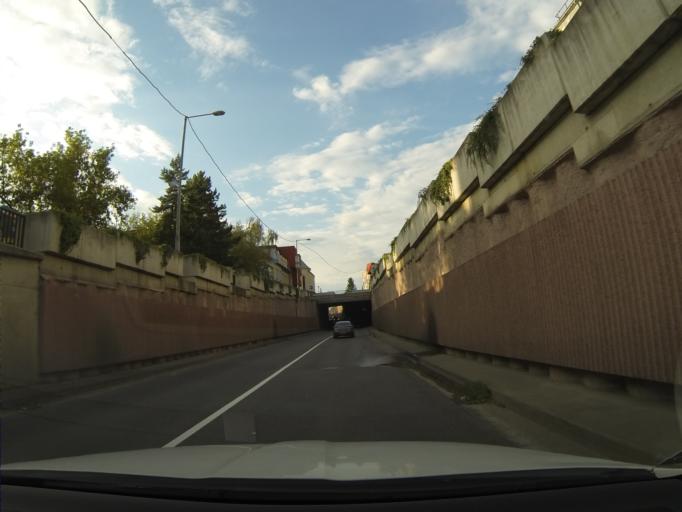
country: SK
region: Nitriansky
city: Prievidza
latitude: 48.7719
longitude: 18.6252
